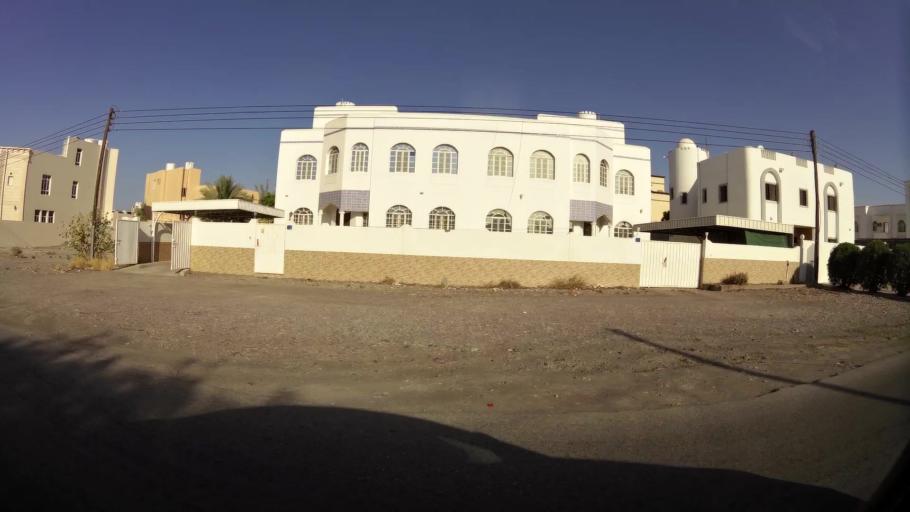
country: OM
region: Muhafazat Masqat
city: As Sib al Jadidah
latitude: 23.6351
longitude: 58.2042
